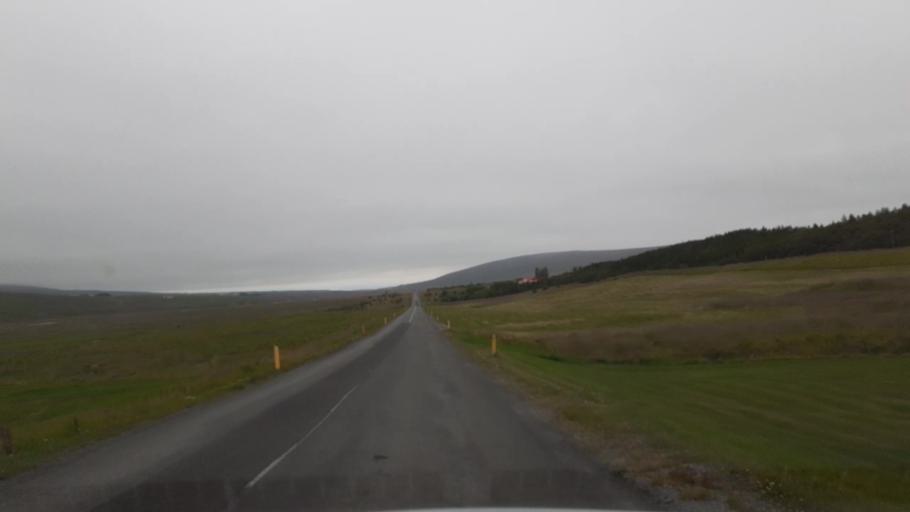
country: IS
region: Northeast
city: Siglufjoerdur
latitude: 65.7333
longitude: -19.1154
